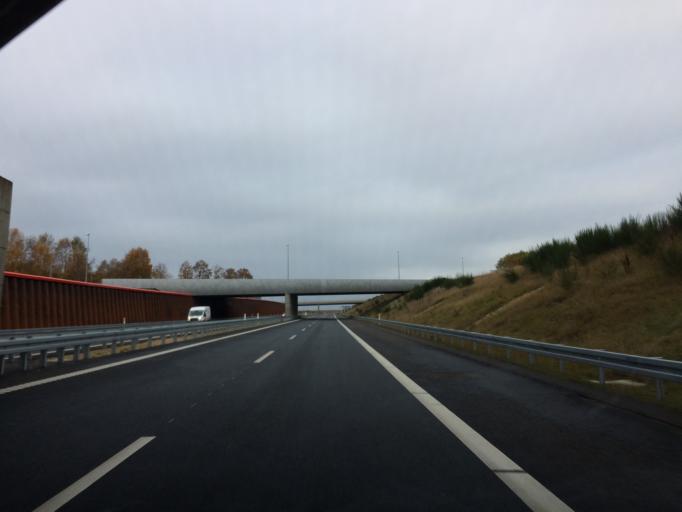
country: DK
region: Central Jutland
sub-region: Silkeborg Kommune
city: Silkeborg
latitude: 56.1950
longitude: 9.5607
